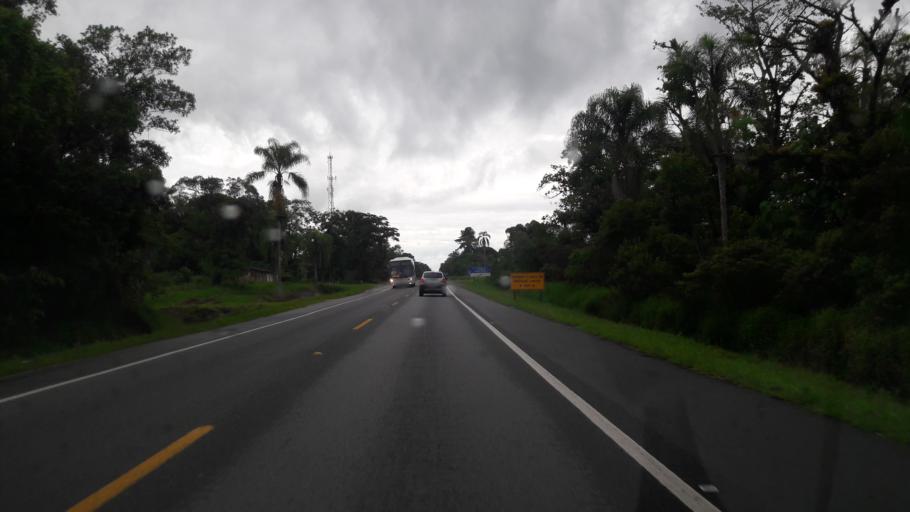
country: BR
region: Parana
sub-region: Pontal Do Parana
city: Pontal do Parana
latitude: -25.6438
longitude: -48.5313
